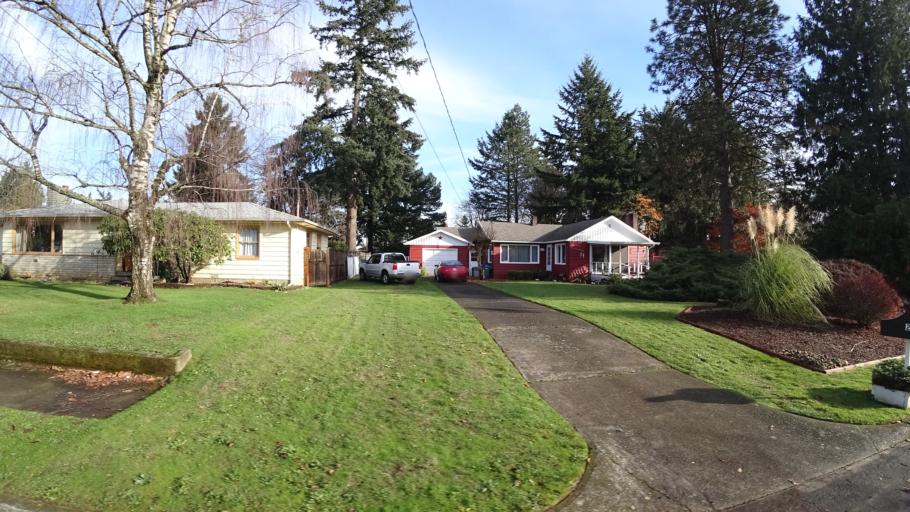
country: US
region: Oregon
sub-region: Multnomah County
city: Lents
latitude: 45.5210
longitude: -122.5309
